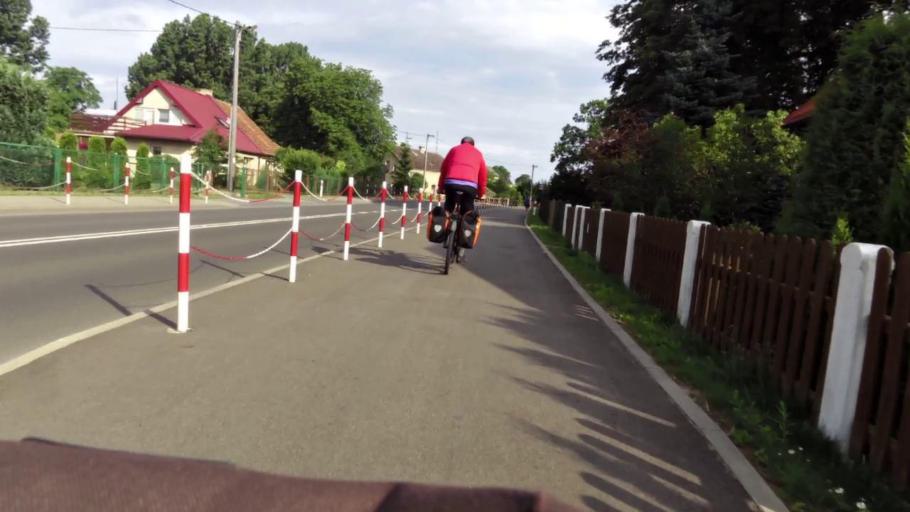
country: PL
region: West Pomeranian Voivodeship
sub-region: Powiat kamienski
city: Dziwnow
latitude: 54.0126
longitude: 14.8147
